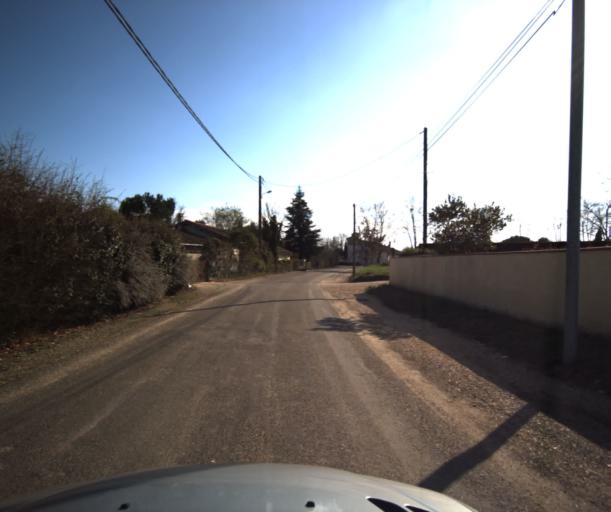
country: FR
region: Midi-Pyrenees
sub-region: Departement du Tarn-et-Garonne
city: Bressols
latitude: 43.9398
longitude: 1.3087
